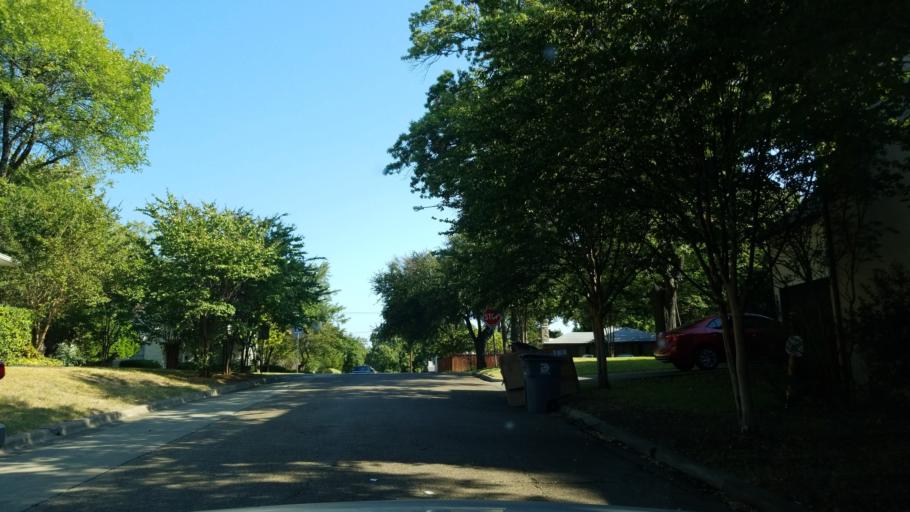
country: US
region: Texas
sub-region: Dallas County
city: Highland Park
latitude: 32.8100
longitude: -96.7361
